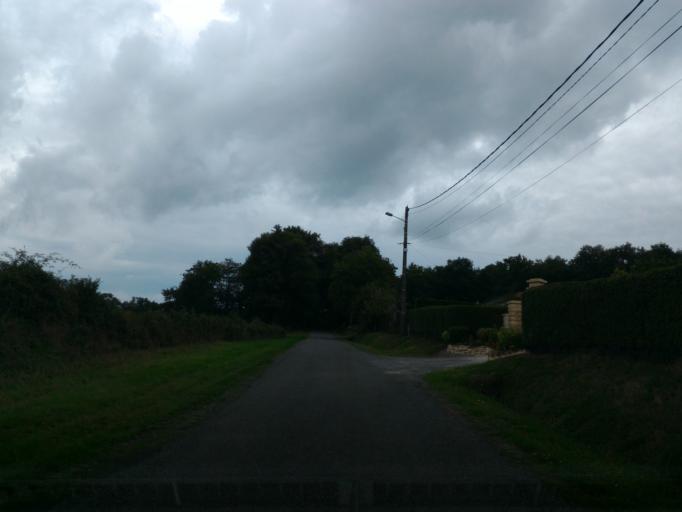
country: FR
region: Poitou-Charentes
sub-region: Departement de la Charente
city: Chabanais
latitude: 45.8931
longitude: 0.7438
